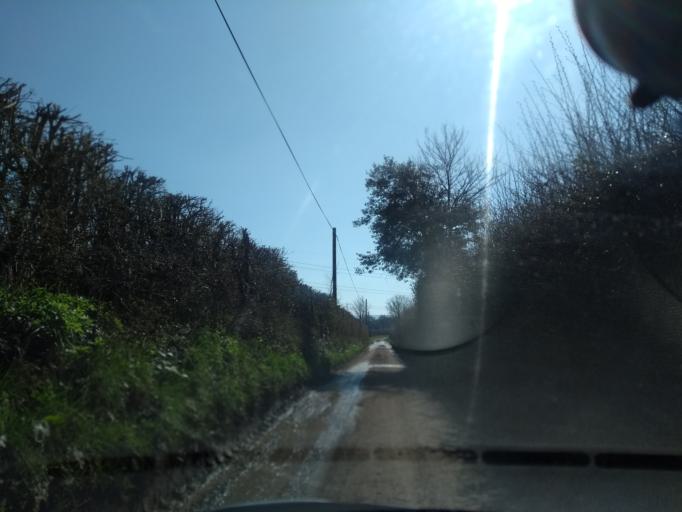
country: GB
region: England
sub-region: Somerset
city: Taunton
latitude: 51.0459
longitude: -3.1182
